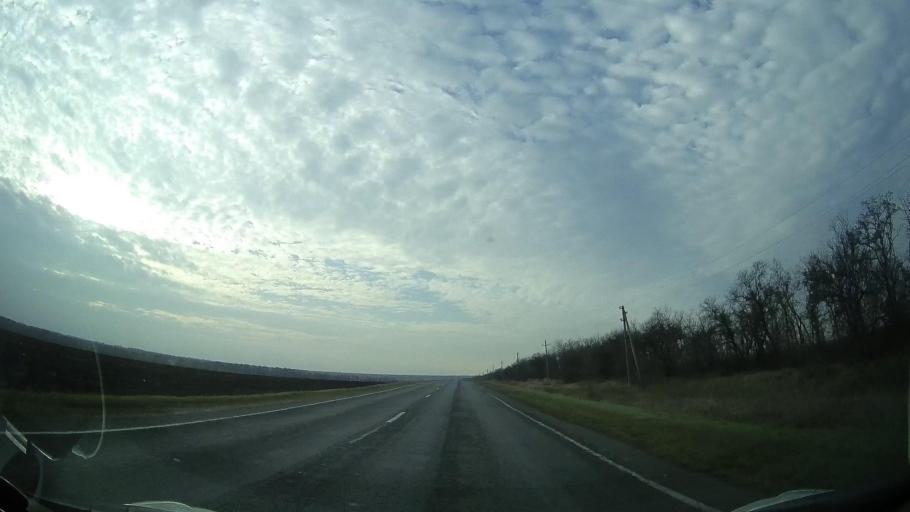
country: RU
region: Rostov
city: Bagayevskaya
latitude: 47.0927
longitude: 40.3401
